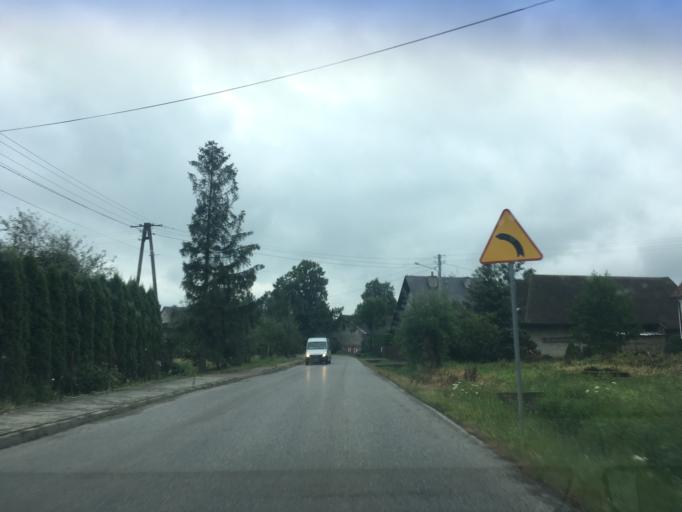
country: PL
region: Lesser Poland Voivodeship
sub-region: Powiat myslenicki
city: Lipnik
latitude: 49.7992
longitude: 20.0951
